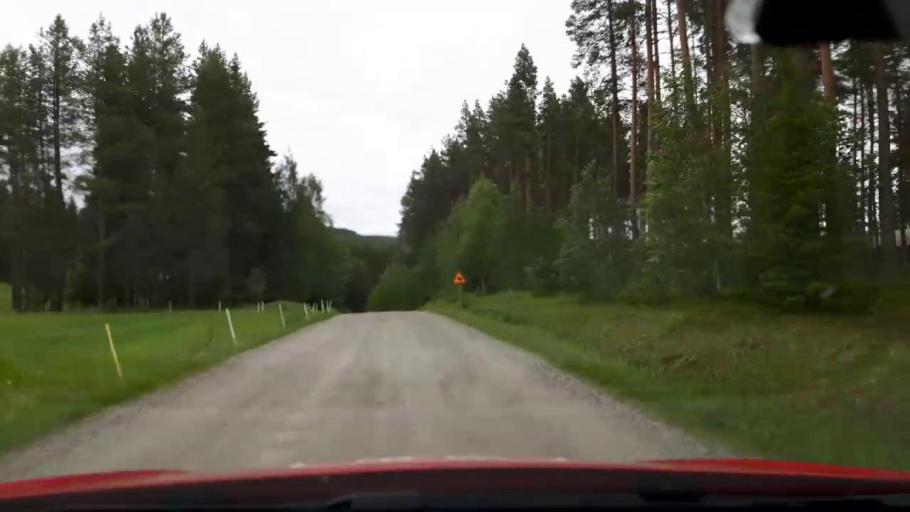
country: SE
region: Jaemtland
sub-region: Ragunda Kommun
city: Hammarstrand
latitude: 63.2105
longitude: 16.0998
